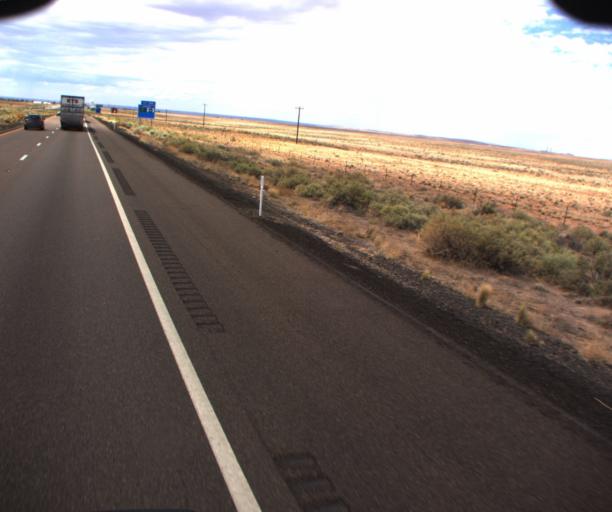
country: US
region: Arizona
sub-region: Navajo County
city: Holbrook
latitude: 34.9524
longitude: -110.1156
